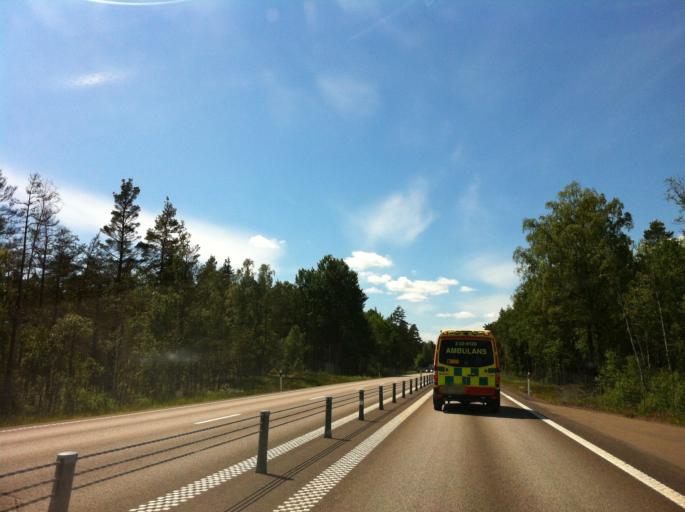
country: SE
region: Vaestra Goetaland
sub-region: Melleruds Kommun
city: Mellerud
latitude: 58.8392
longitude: 12.5427
